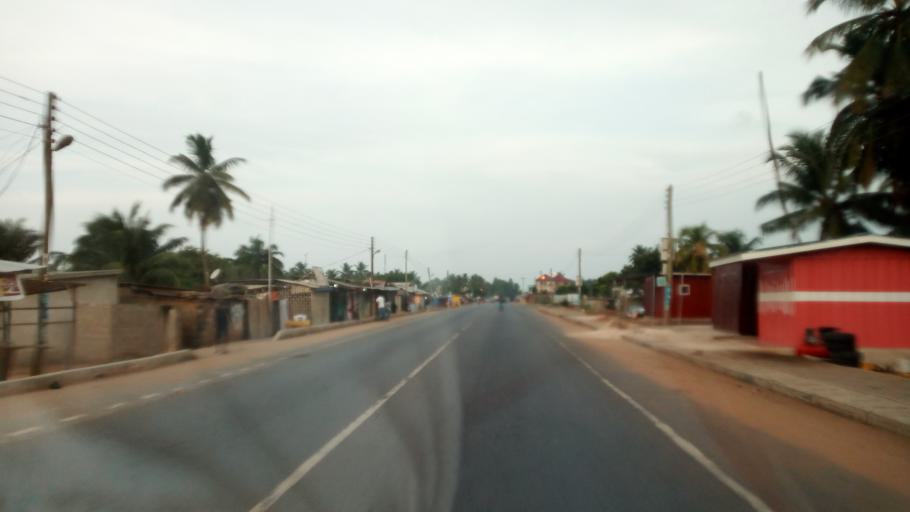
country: TG
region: Maritime
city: Lome
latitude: 6.1161
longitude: 1.1715
